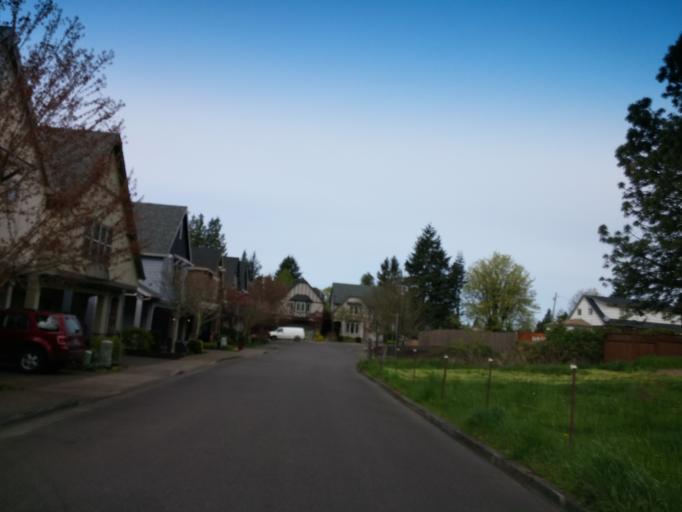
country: US
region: Oregon
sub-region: Washington County
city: Cedar Mill
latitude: 45.5379
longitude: -122.7975
